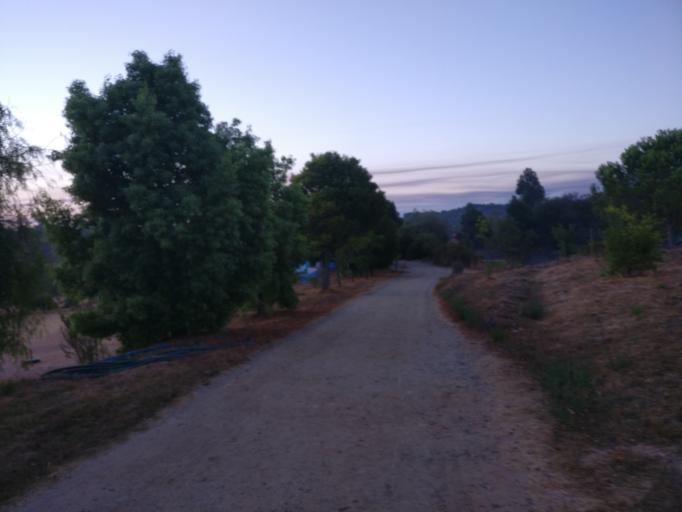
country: PT
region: Beja
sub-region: Odemira
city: Odemira
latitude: 37.7189
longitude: -8.5205
